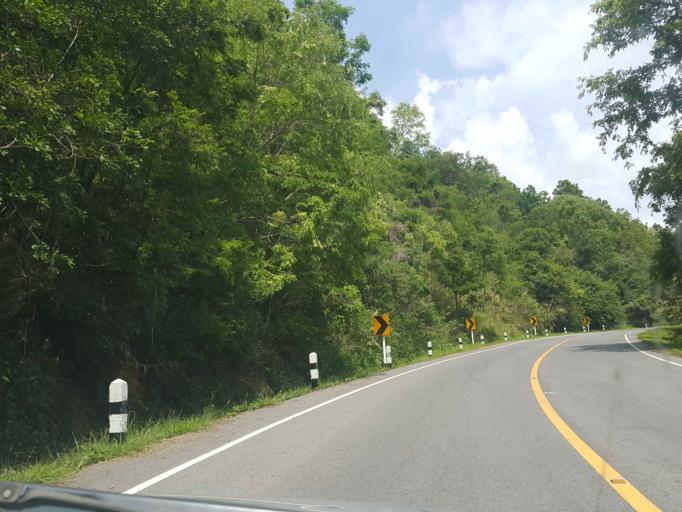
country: TH
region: Nan
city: Ban Luang
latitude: 18.8751
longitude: 100.4876
